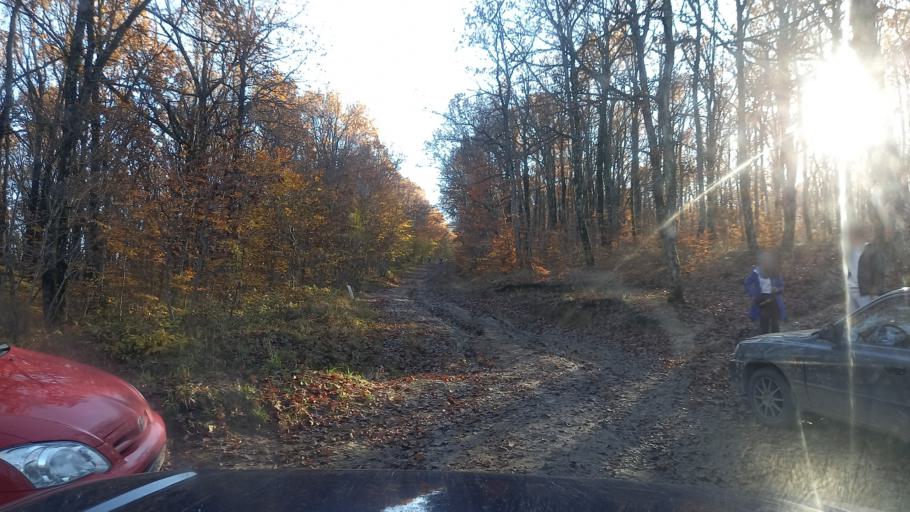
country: RU
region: Krasnodarskiy
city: Goryachiy Klyuch
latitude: 44.6168
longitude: 39.1044
